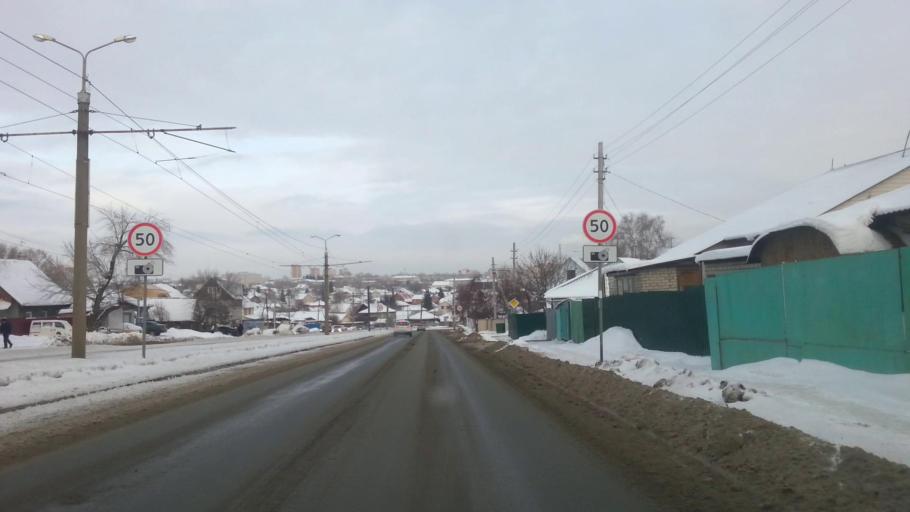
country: RU
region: Altai Krai
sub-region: Gorod Barnaulskiy
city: Barnaul
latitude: 53.3648
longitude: 83.7303
